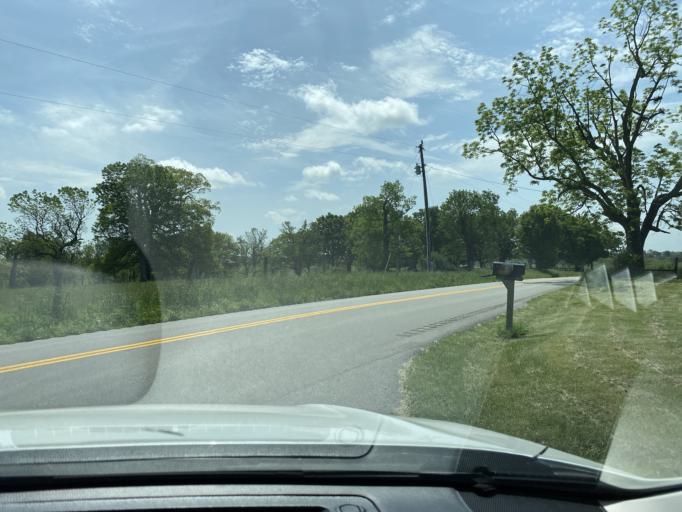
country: US
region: Kentucky
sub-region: Scott County
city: Georgetown
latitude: 38.2528
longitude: -84.5901
